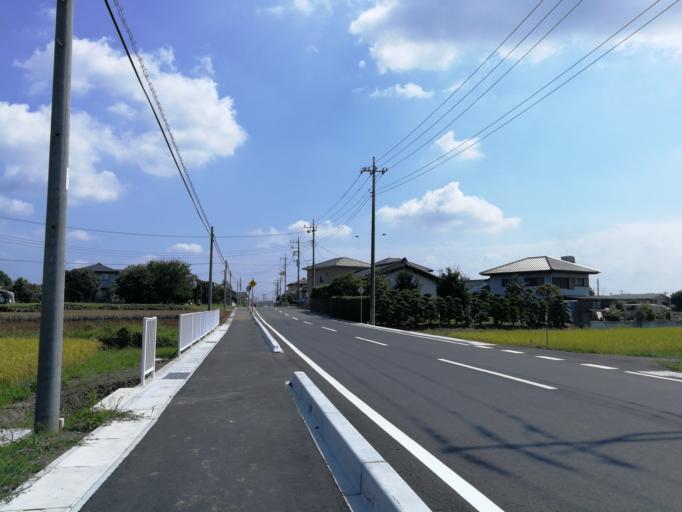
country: JP
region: Ibaraki
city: Tomobe
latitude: 36.3700
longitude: 140.3437
